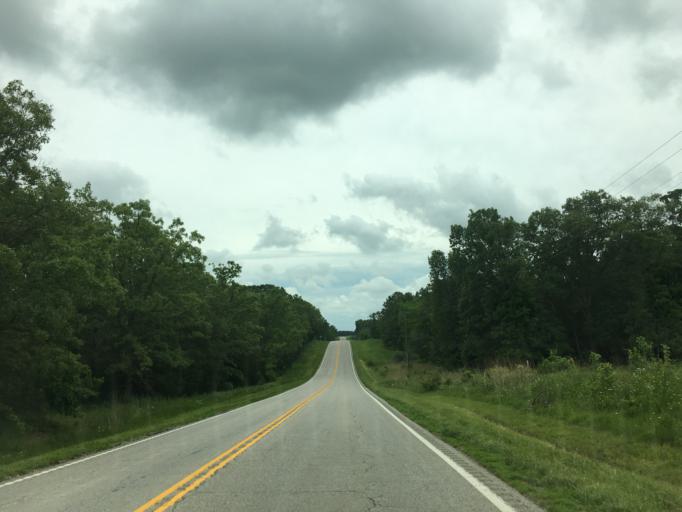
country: US
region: Missouri
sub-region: Gasconade County
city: Owensville
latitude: 38.4886
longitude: -91.4620
